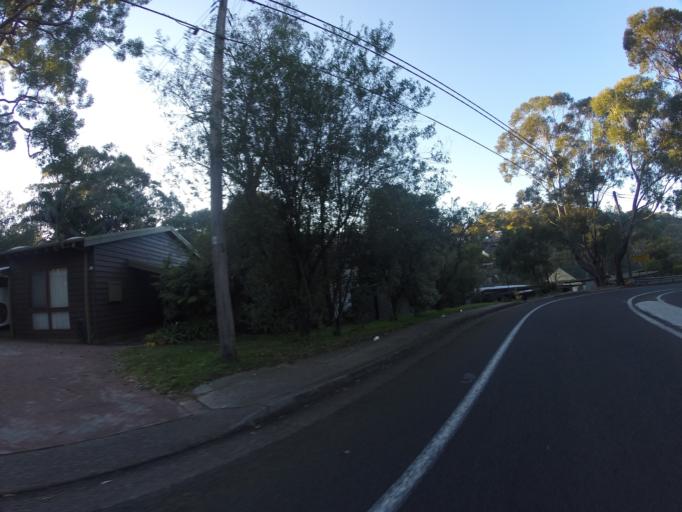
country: AU
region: New South Wales
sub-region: Sutherland Shire
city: Gymea Bay
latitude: -34.0483
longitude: 151.0766
